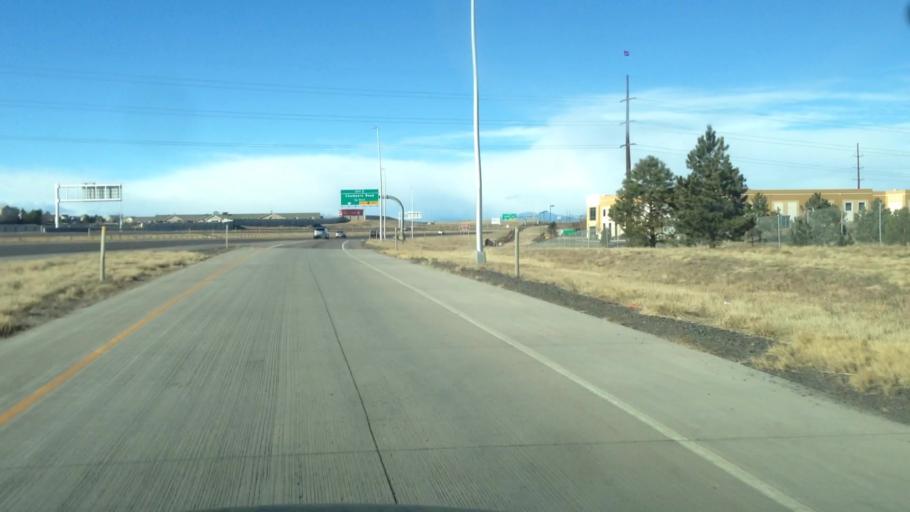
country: US
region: Colorado
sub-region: Douglas County
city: Stonegate
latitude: 39.5495
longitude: -104.7970
